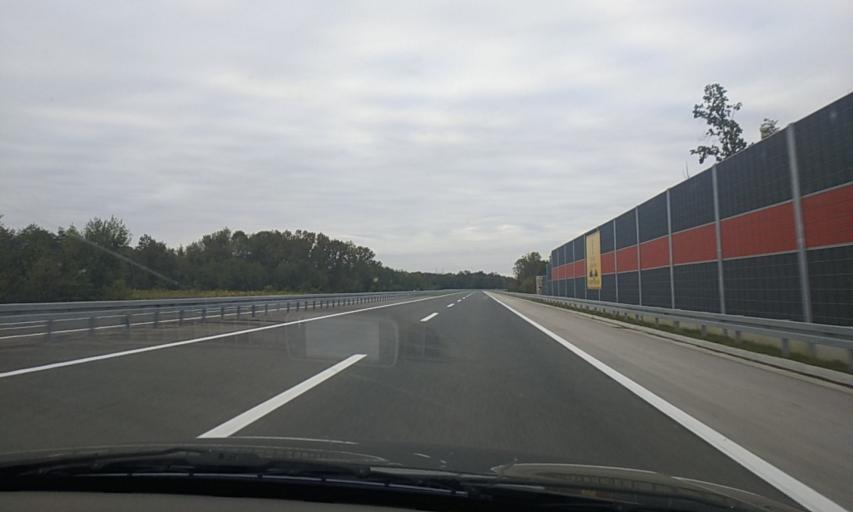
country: BA
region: Republika Srpska
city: Maglajani
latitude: 44.8843
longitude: 17.3781
